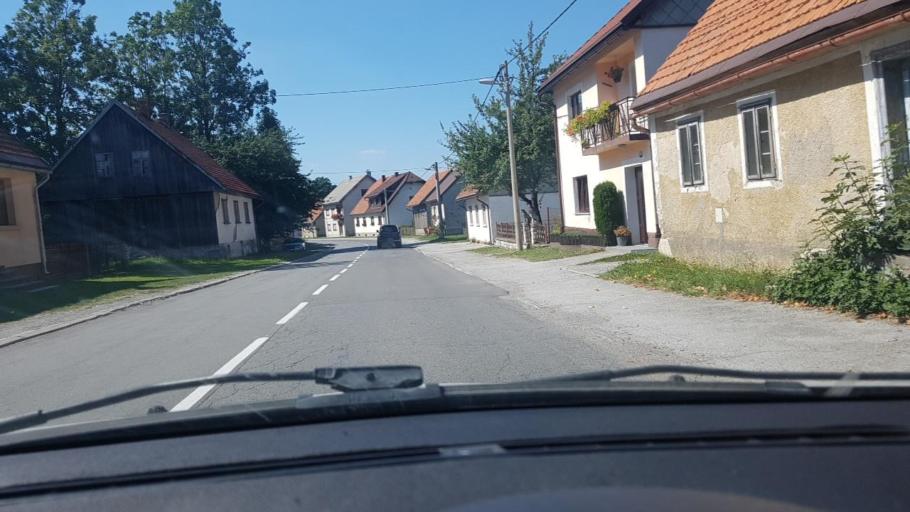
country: HR
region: Primorsko-Goranska
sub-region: Grad Delnice
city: Delnice
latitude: 45.3737
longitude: 14.9295
